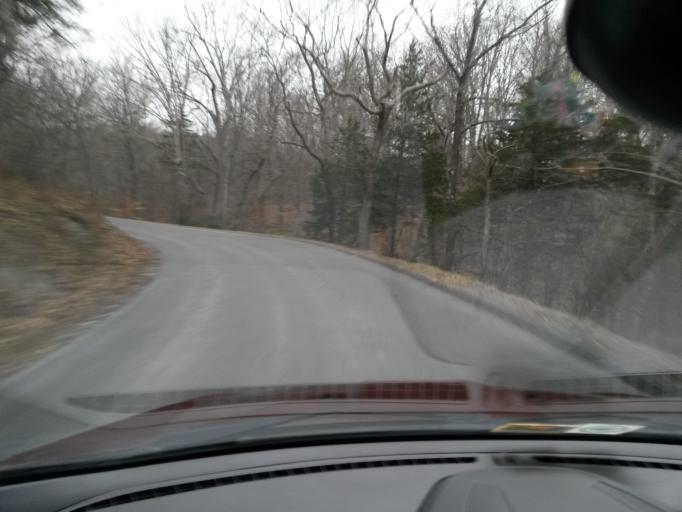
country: US
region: Virginia
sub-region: Rockbridge County
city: East Lexington
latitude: 37.9436
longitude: -79.2770
